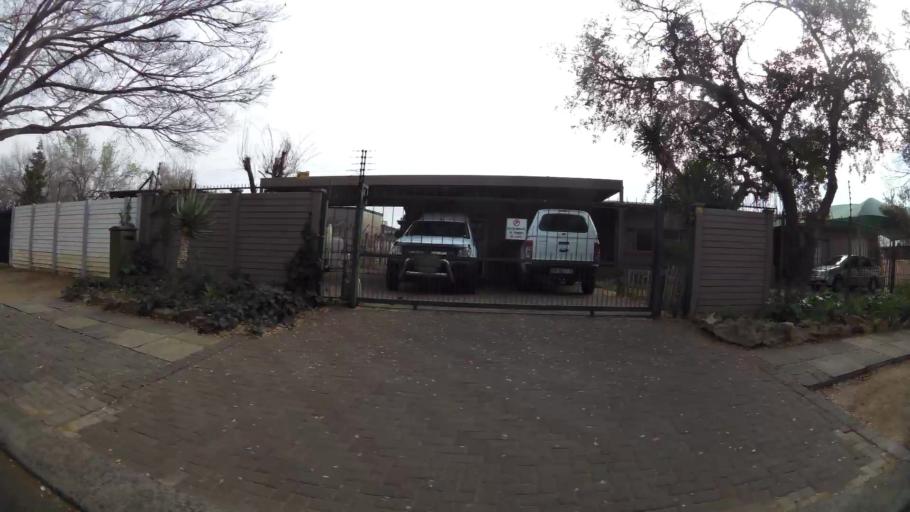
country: ZA
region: Orange Free State
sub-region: Mangaung Metropolitan Municipality
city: Bloemfontein
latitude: -29.1222
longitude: 26.1846
